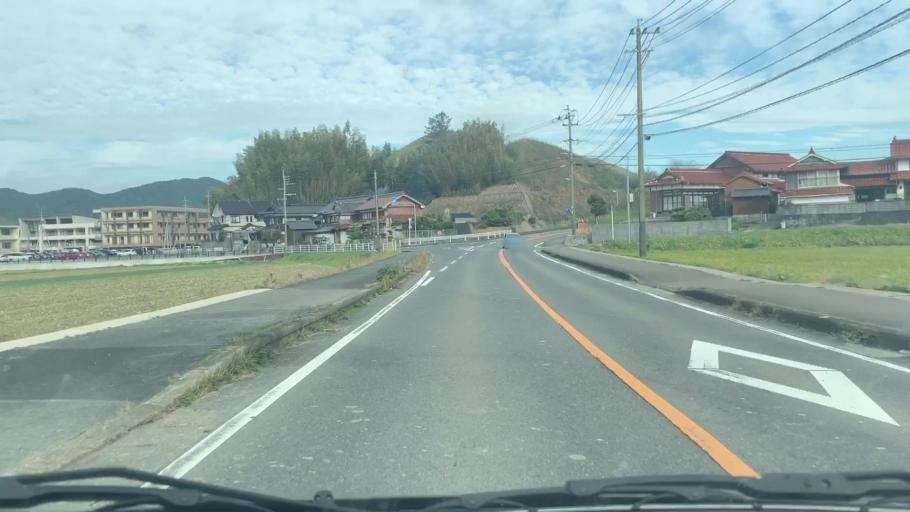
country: JP
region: Saga Prefecture
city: Karatsu
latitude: 33.3944
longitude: 129.9863
